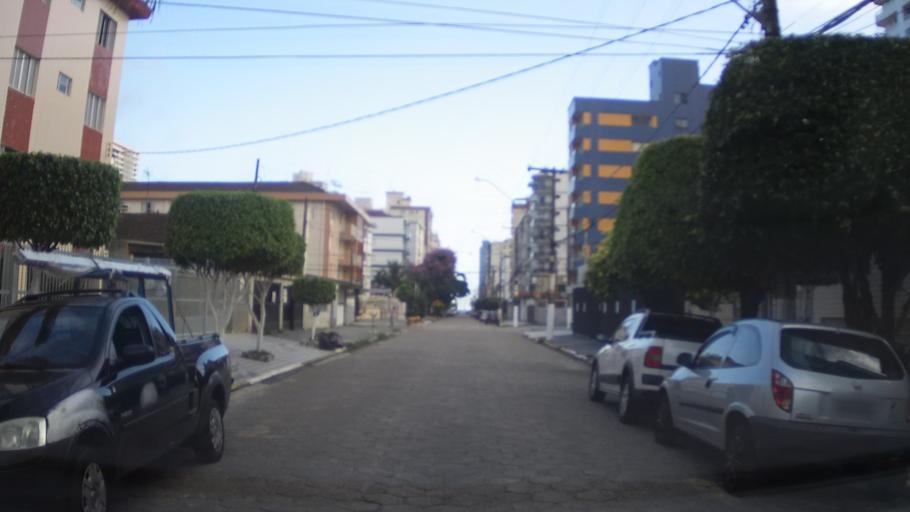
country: BR
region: Sao Paulo
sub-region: Praia Grande
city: Praia Grande
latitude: -24.0090
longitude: -46.4091
